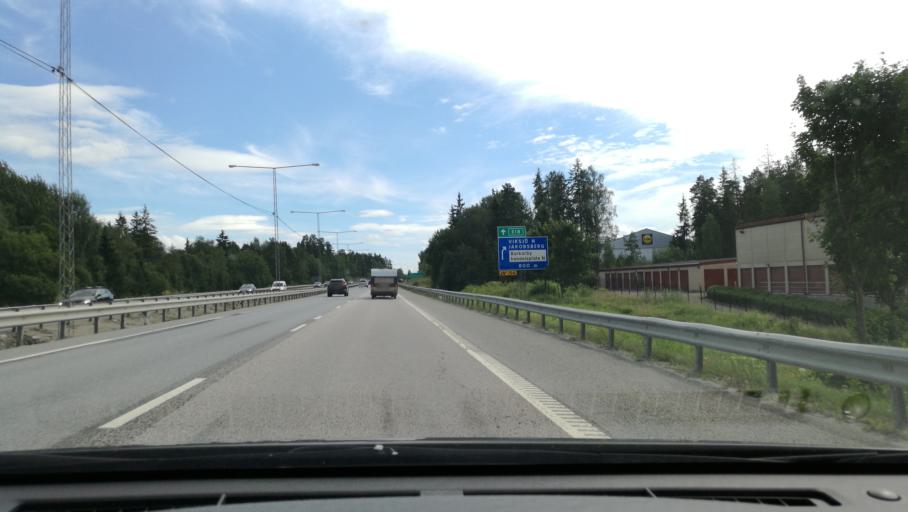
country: SE
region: Stockholm
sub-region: Jarfalla Kommun
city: Jakobsberg
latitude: 59.4314
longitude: 17.8471
